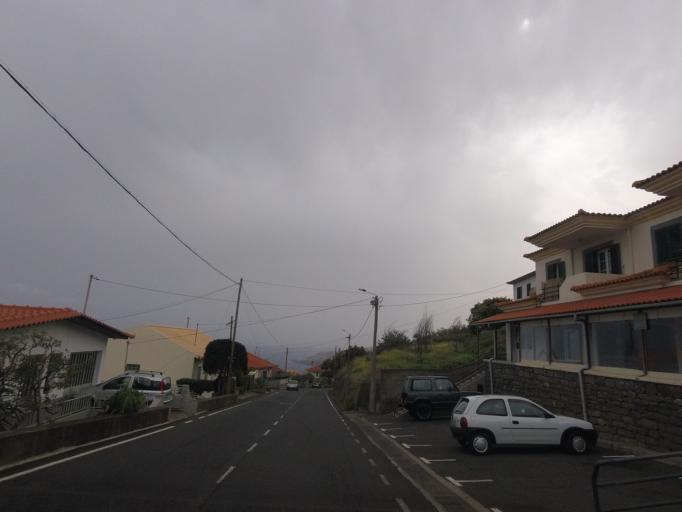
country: PT
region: Madeira
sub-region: Machico
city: Machico
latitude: 32.7007
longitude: -16.7815
